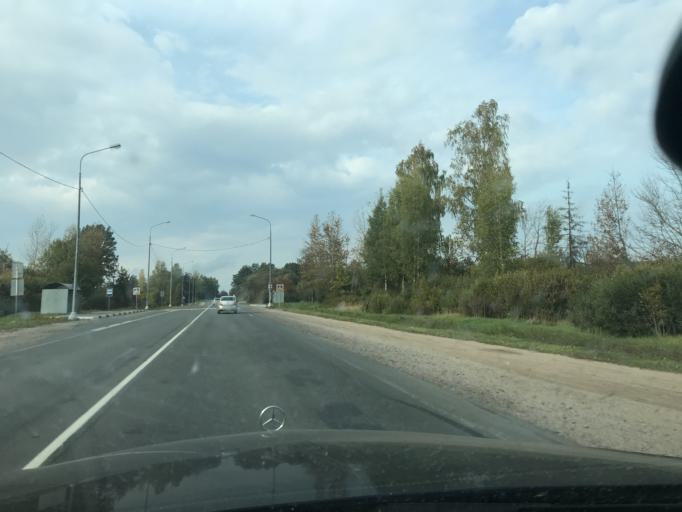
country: RU
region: Pskov
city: Ostrov
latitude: 57.3006
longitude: 28.3739
